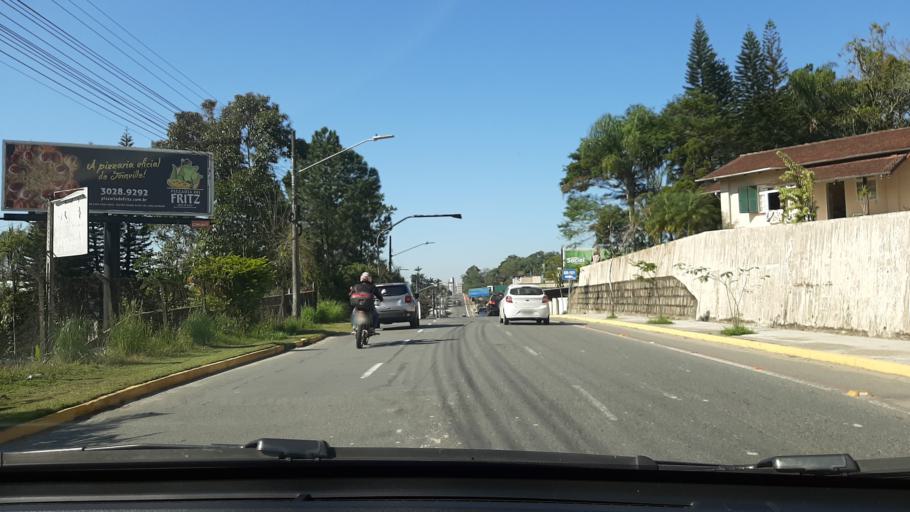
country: BR
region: Santa Catarina
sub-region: Joinville
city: Joinville
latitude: -26.3134
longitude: -48.8624
